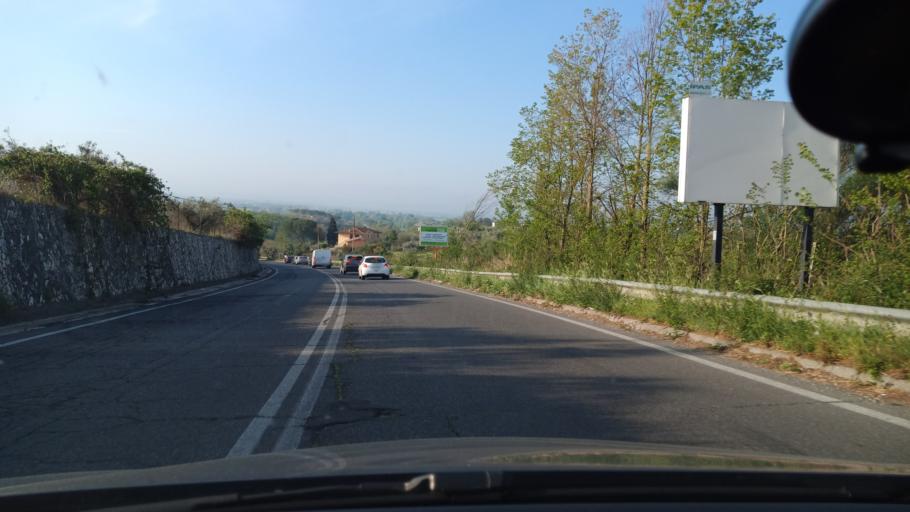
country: IT
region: Latium
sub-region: Citta metropolitana di Roma Capitale
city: Fiano Romano
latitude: 42.1805
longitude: 12.6358
